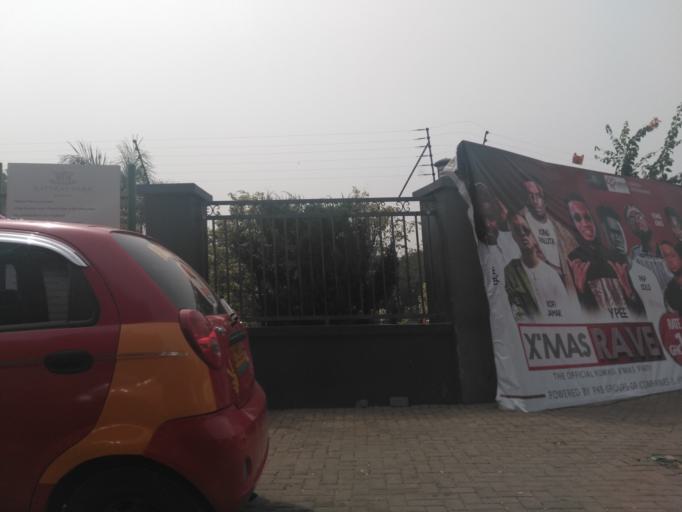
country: GH
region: Ashanti
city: Kumasi
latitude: 6.6815
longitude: -1.6249
